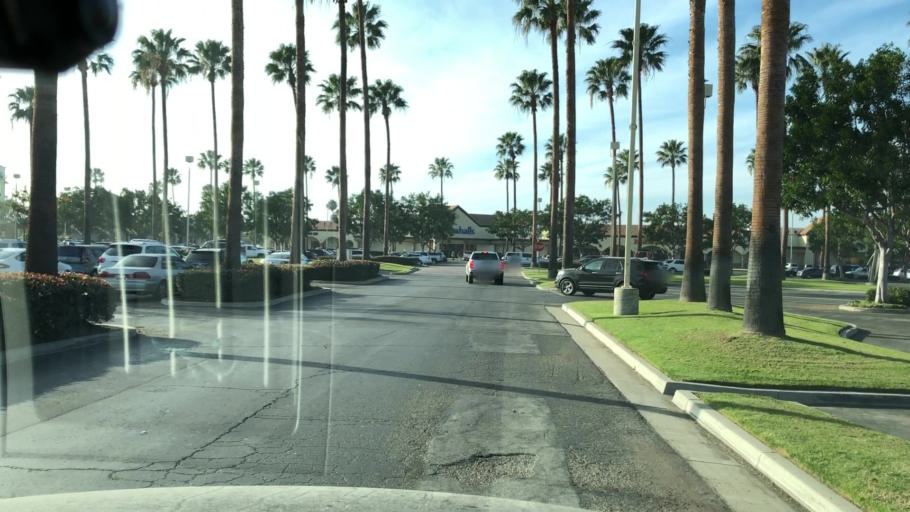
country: US
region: California
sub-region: Ventura County
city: El Rio
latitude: 34.2248
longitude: -119.1510
